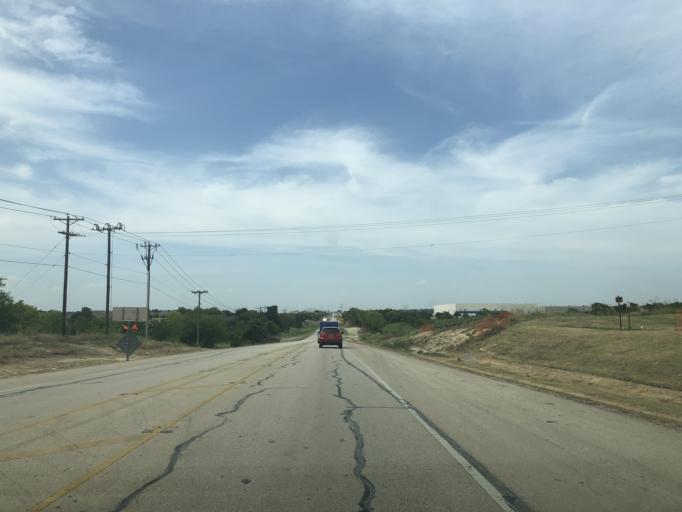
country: US
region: Texas
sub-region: Tarrant County
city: Saginaw
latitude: 32.9024
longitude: -97.3488
